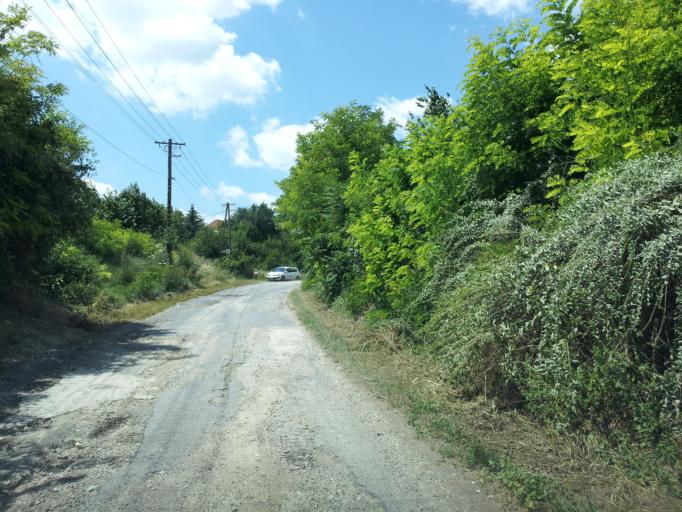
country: HU
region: Veszprem
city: Balatonkenese
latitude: 47.0383
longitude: 18.0981
